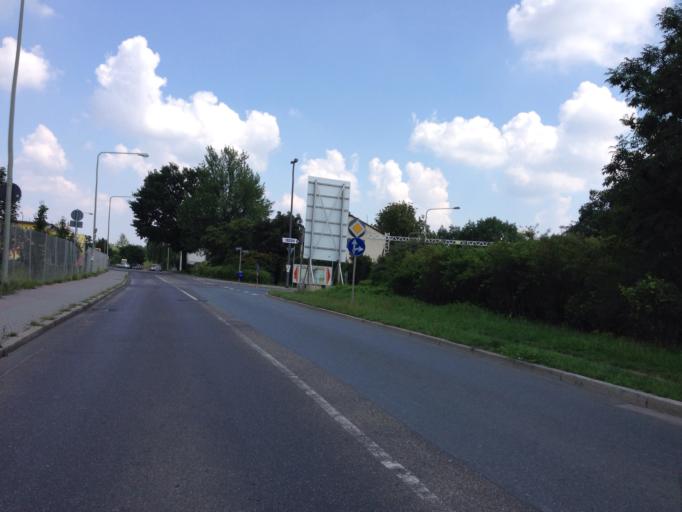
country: DE
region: Hesse
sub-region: Regierungsbezirk Darmstadt
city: Offenbach
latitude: 50.1145
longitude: 8.7616
